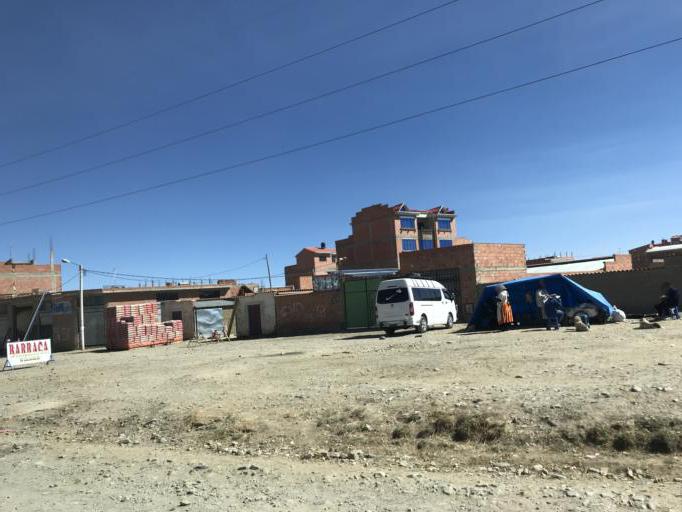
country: BO
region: La Paz
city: La Paz
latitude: -16.5006
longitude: -68.2377
